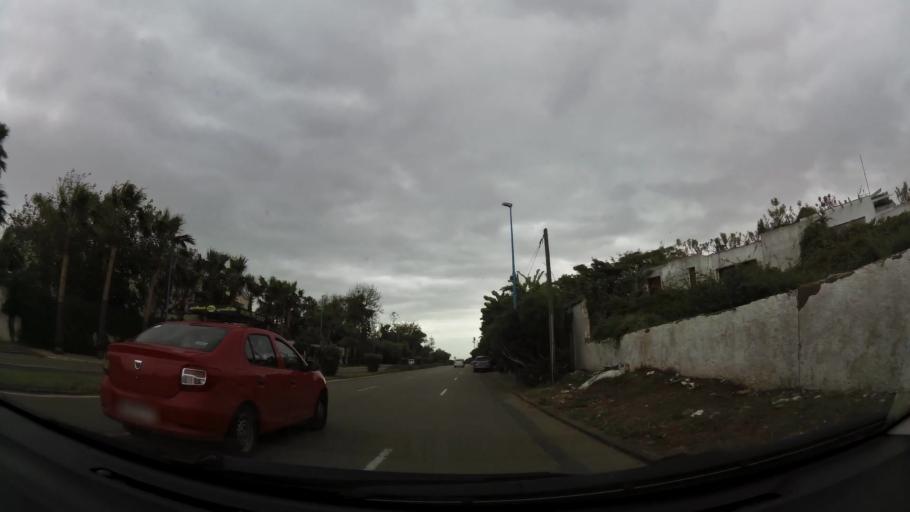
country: MA
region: Grand Casablanca
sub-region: Casablanca
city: Casablanca
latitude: 33.5839
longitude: -7.6706
